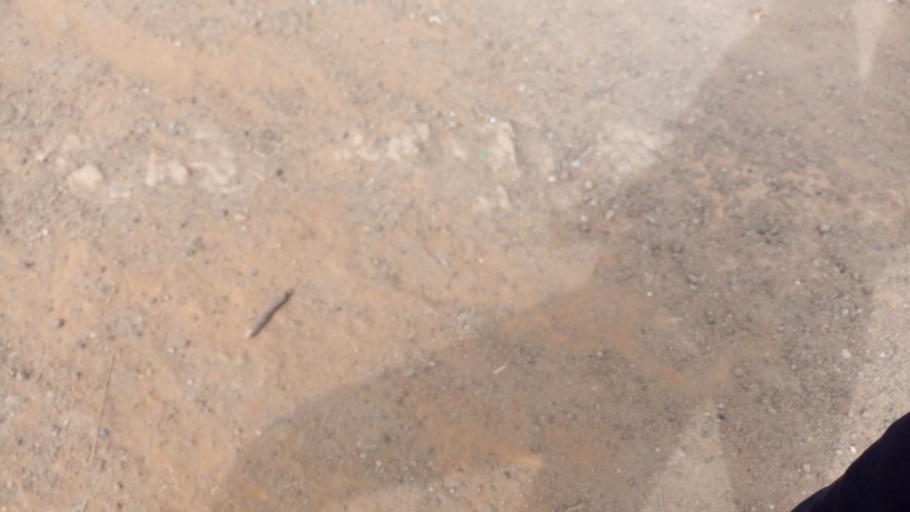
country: CI
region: Vallee du Bandama
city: Bouake
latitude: 7.7014
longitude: -5.0291
